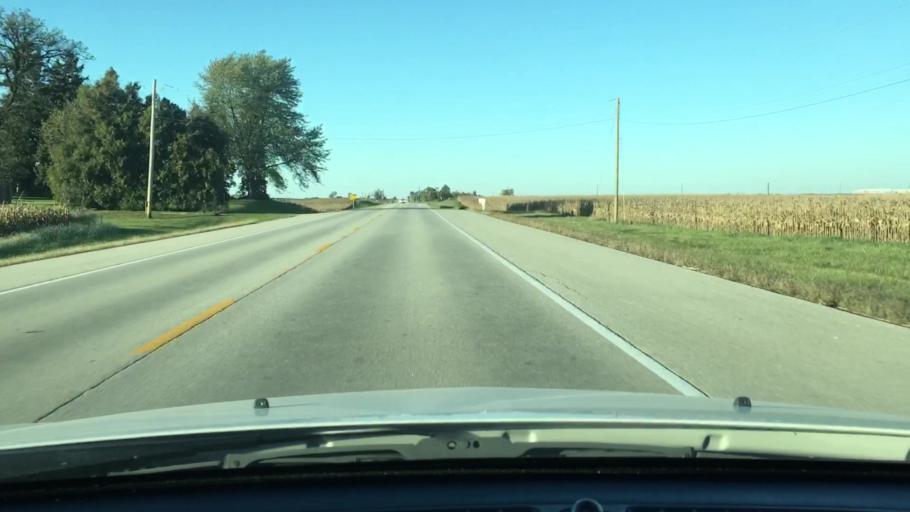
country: US
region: Illinois
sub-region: DeKalb County
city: Waterman
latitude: 41.8094
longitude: -88.7539
